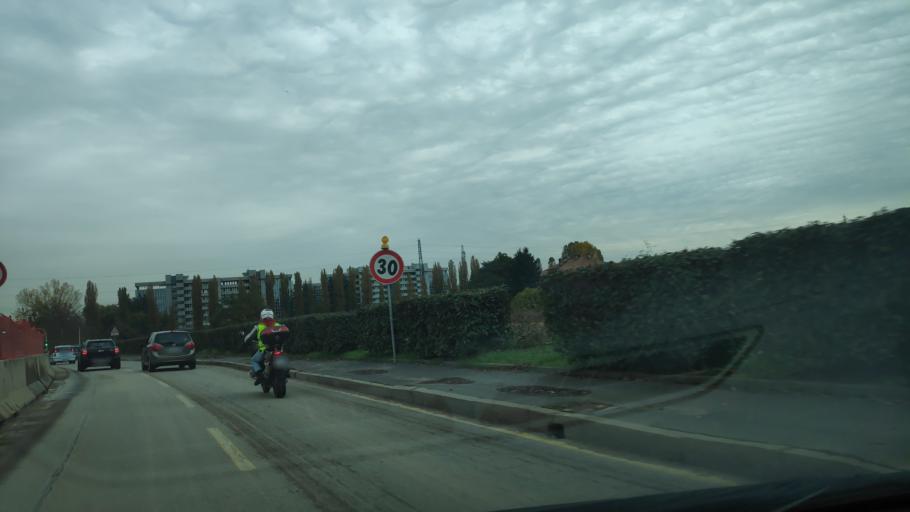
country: IT
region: Lombardy
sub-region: Citta metropolitana di Milano
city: Rozzano
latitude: 45.4051
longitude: 9.1754
